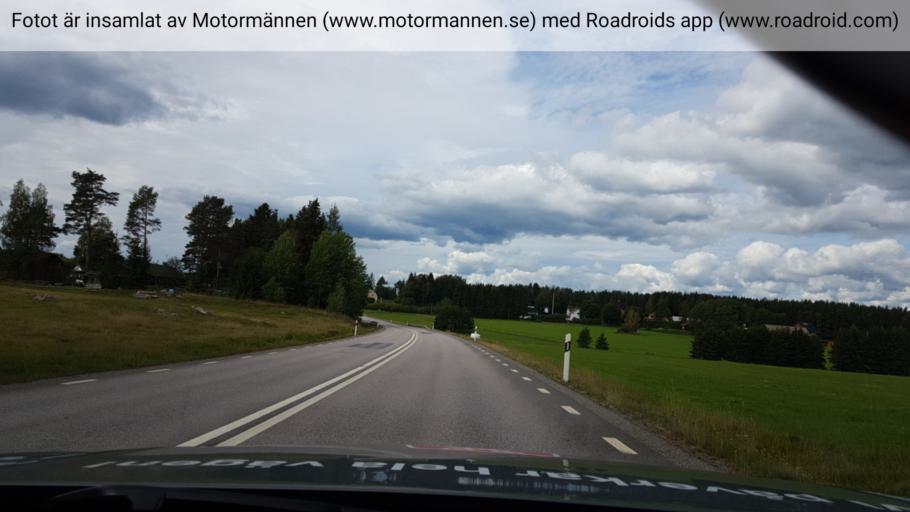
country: SE
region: Uppsala
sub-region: Heby Kommun
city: Morgongava
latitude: 59.9039
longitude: 17.0724
